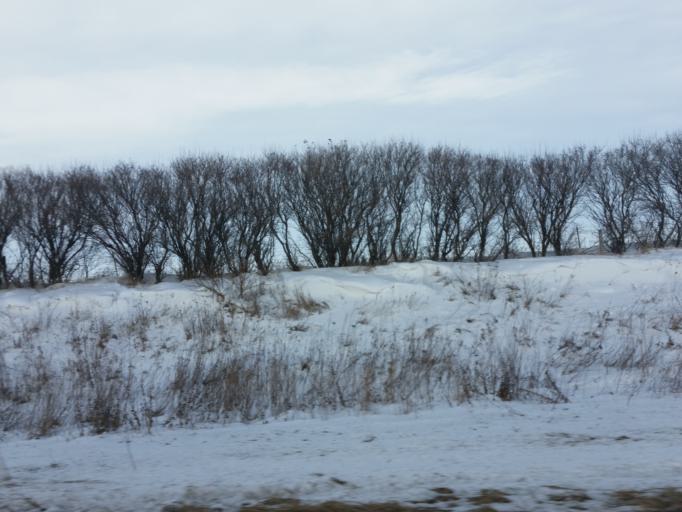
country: US
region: Iowa
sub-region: Delaware County
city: Manchester
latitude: 42.4646
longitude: -91.6223
